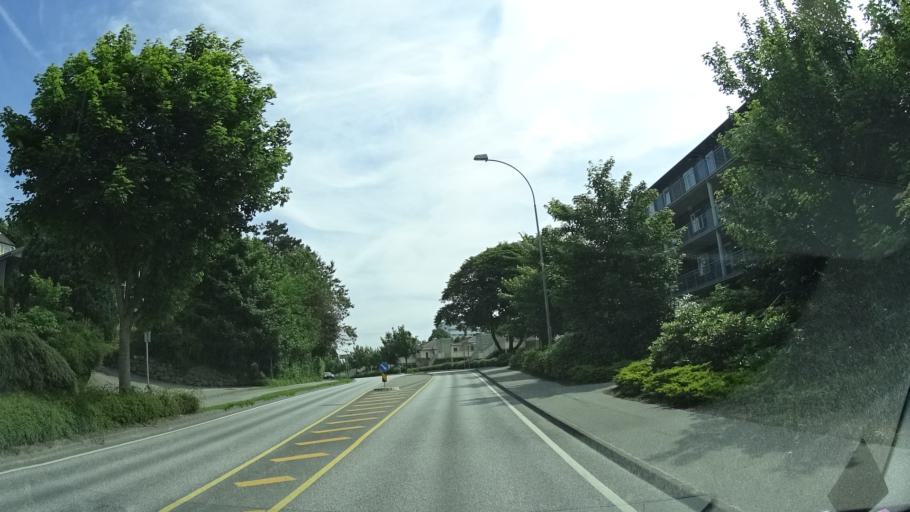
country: NO
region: Rogaland
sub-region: Stavanger
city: Stavanger
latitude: 58.9794
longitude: 5.6927
